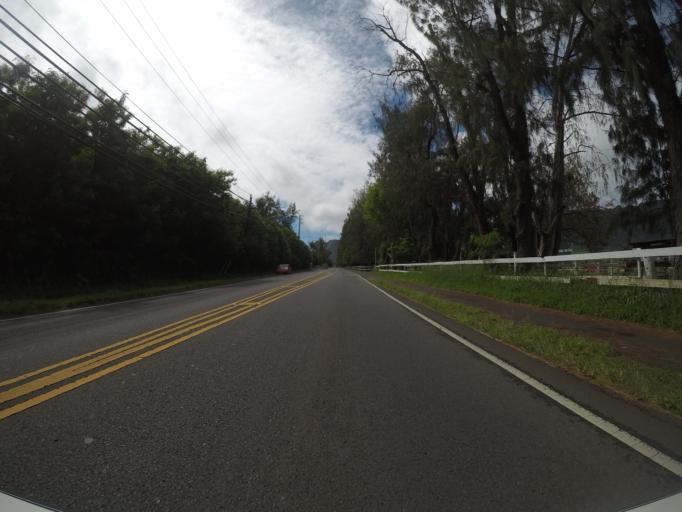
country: US
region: Hawaii
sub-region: Honolulu County
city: Waimanalo Beach
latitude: 21.3438
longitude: -157.7085
